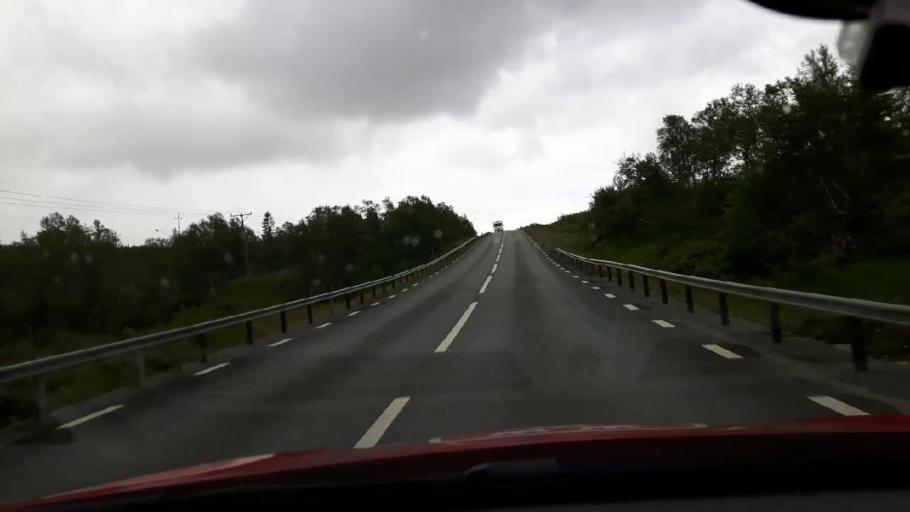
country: NO
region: Nord-Trondelag
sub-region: Meraker
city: Meraker
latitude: 63.3194
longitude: 12.0774
